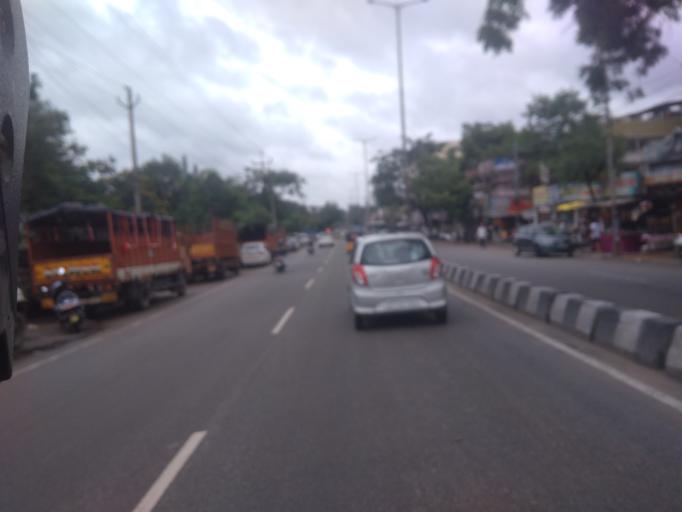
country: IN
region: Telangana
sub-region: Rangareddi
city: Secunderabad
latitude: 17.5012
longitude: 78.5139
